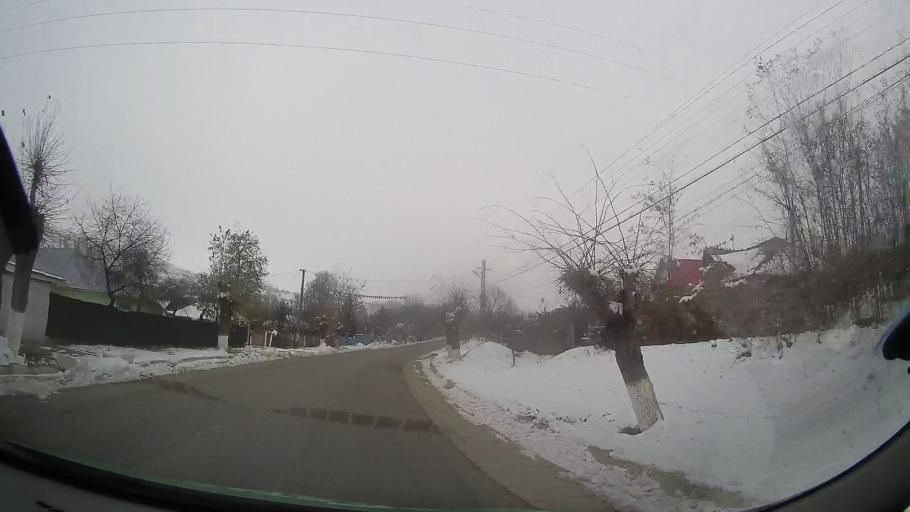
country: RO
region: Bacau
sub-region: Comuna Glavanesti
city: Frumuselu
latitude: 46.2966
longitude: 27.3001
